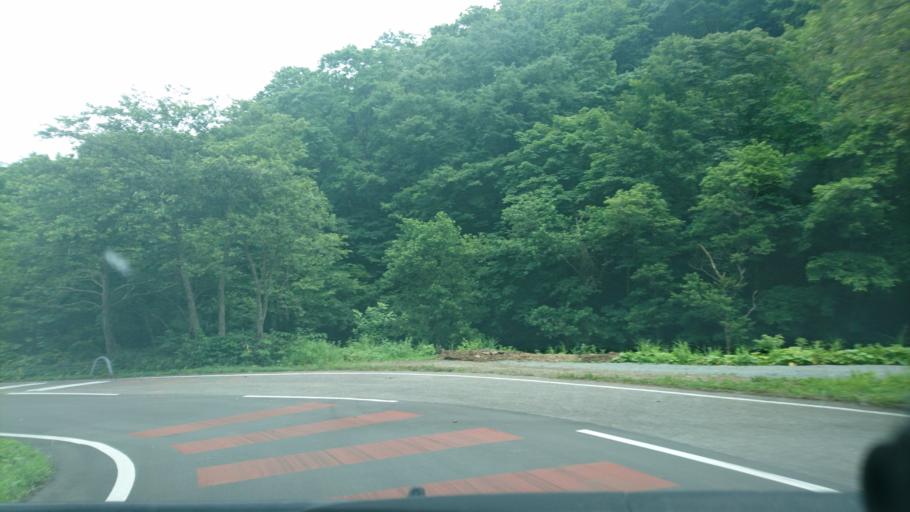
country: JP
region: Akita
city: Yuzawa
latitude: 39.1664
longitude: 140.7459
